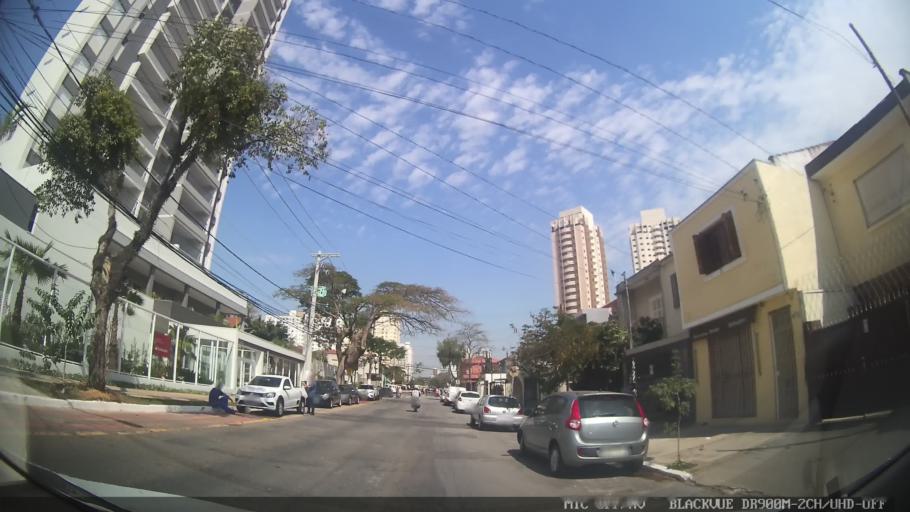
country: BR
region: Sao Paulo
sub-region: Sao Paulo
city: Sao Paulo
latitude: -23.5688
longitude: -46.6206
